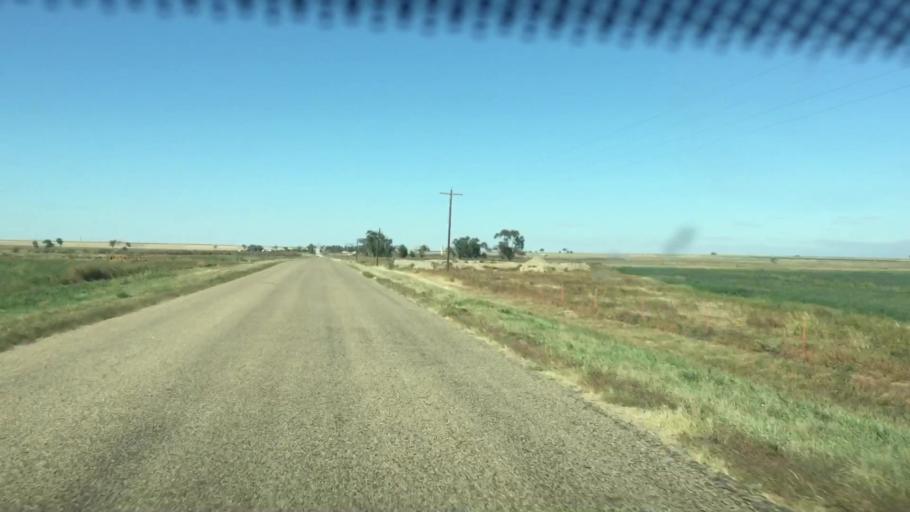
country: US
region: Colorado
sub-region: Prowers County
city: Lamar
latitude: 38.1047
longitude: -102.5214
